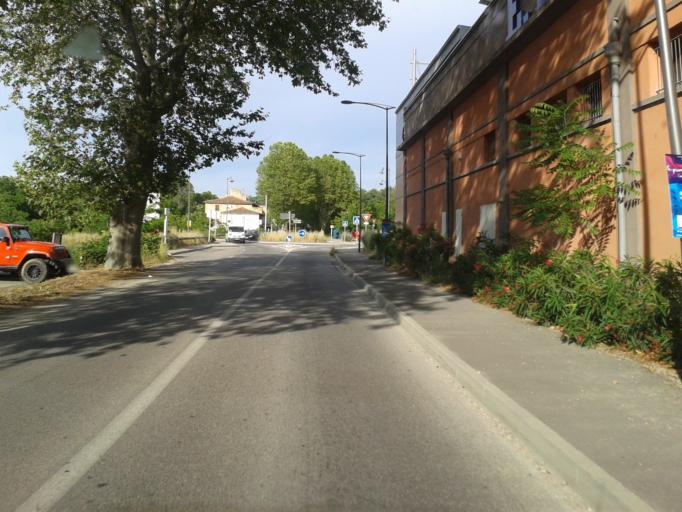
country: FR
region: Provence-Alpes-Cote d'Azur
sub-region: Departement des Bouches-du-Rhone
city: Meyrargues
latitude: 43.6420
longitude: 5.5334
